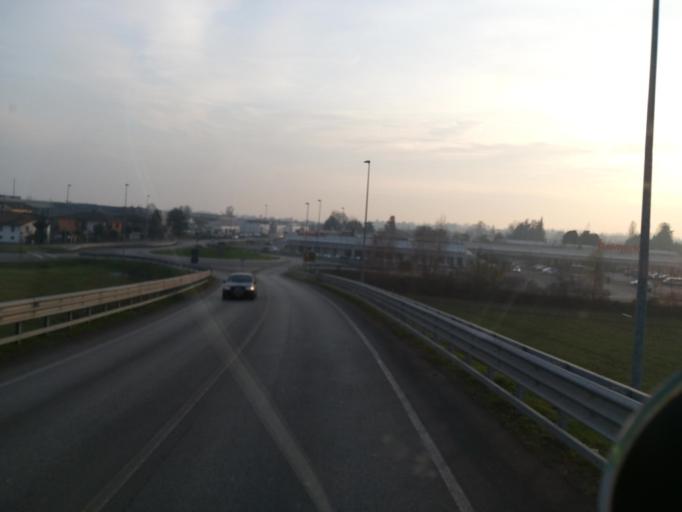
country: IT
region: Lombardy
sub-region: Provincia di Brescia
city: Flero
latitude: 45.4740
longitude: 10.1768
